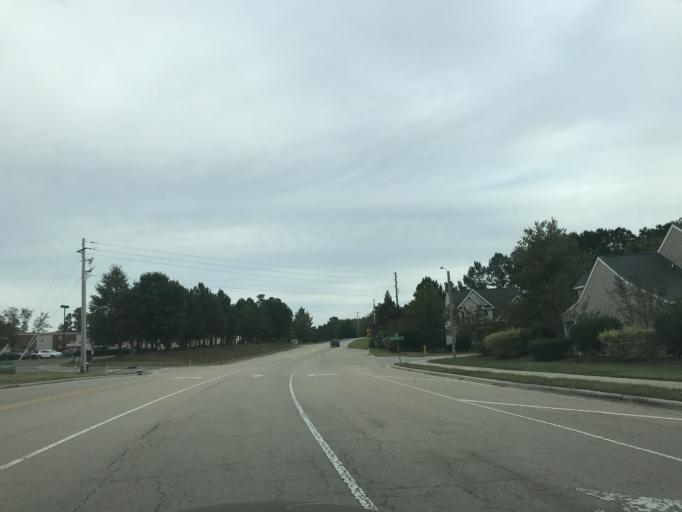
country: US
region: North Carolina
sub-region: Wake County
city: Rolesville
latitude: 35.8926
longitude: -78.5081
